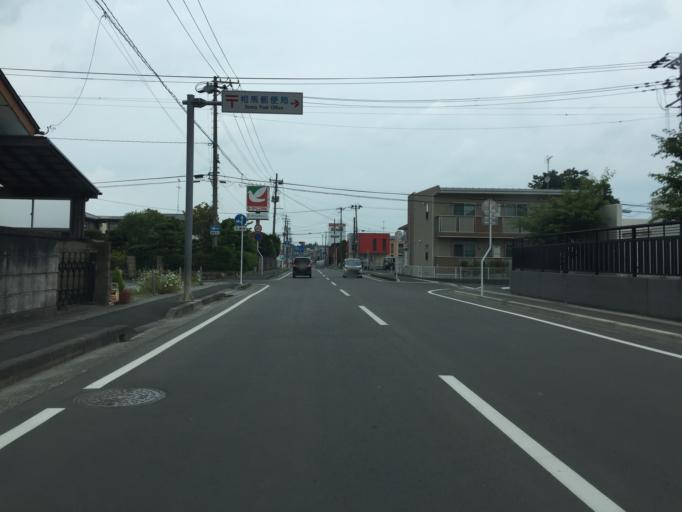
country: JP
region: Miyagi
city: Marumori
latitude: 37.7996
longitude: 140.9178
